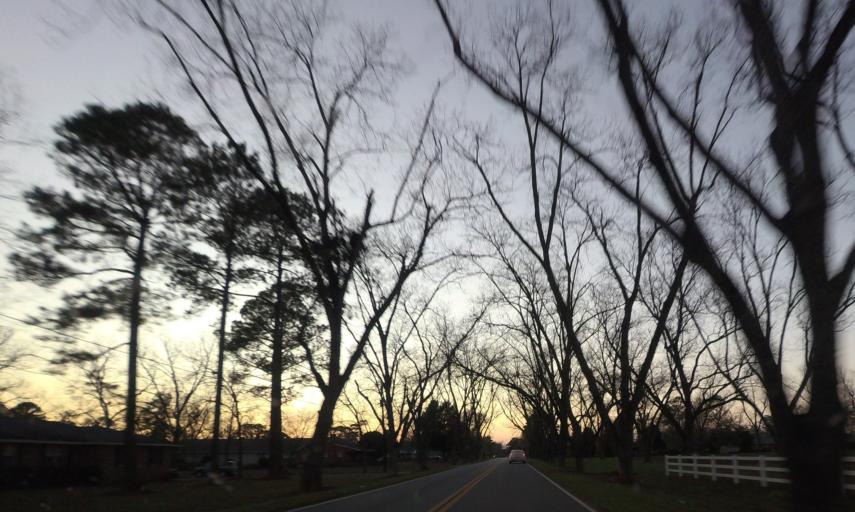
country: US
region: Georgia
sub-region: Houston County
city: Centerville
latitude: 32.7249
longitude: -83.6746
